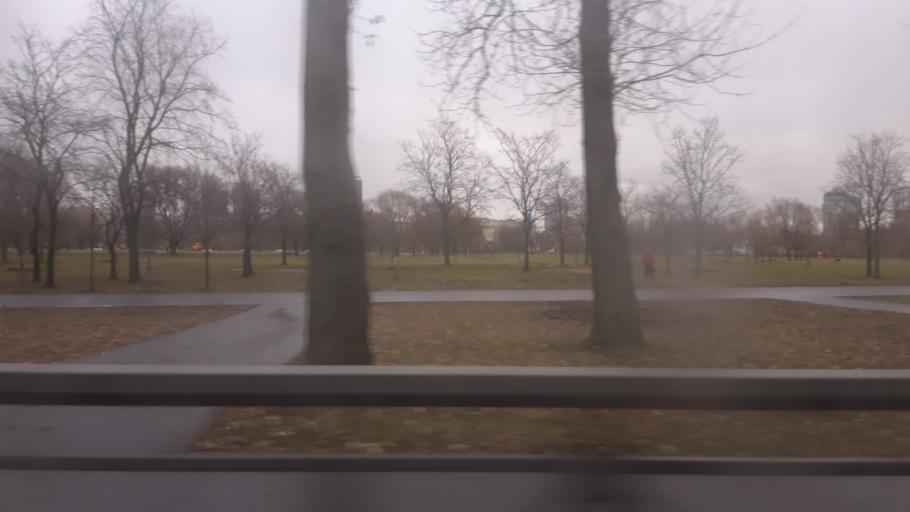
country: RU
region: St.-Petersburg
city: Kupchino
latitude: 59.8379
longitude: 30.3225
